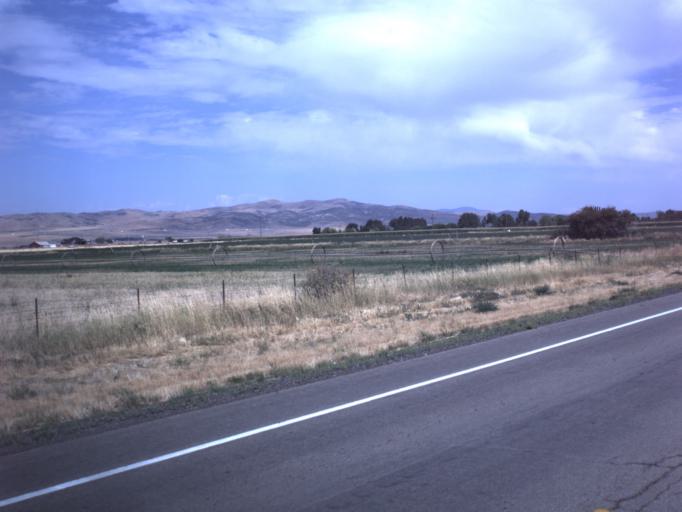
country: US
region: Utah
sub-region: Juab County
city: Nephi
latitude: 39.5442
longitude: -111.8637
